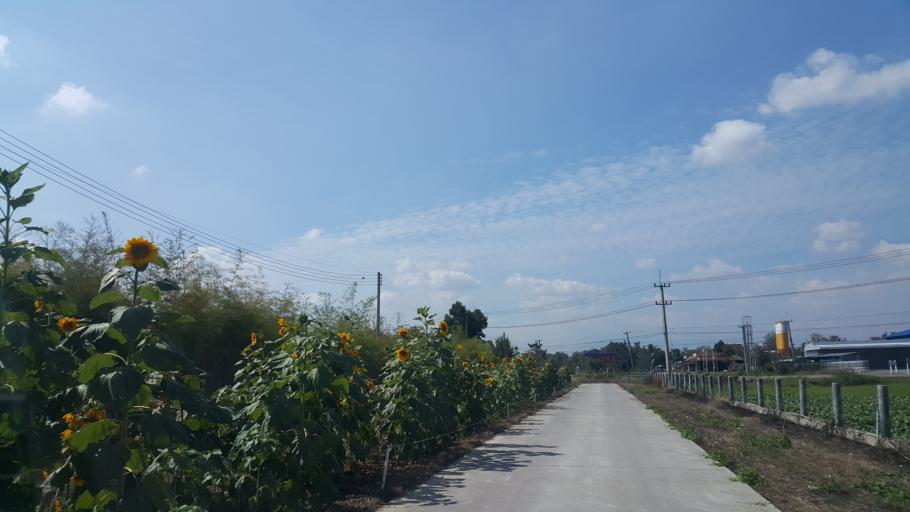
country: TH
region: Chiang Mai
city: San Kamphaeng
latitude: 18.7238
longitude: 99.1643
